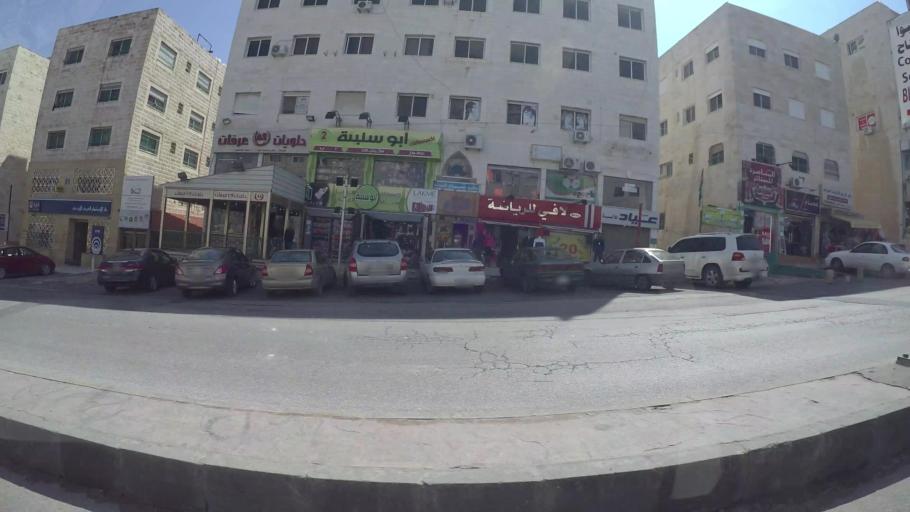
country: JO
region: Amman
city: Al Bunayyat ash Shamaliyah
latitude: 31.9166
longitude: 35.8905
